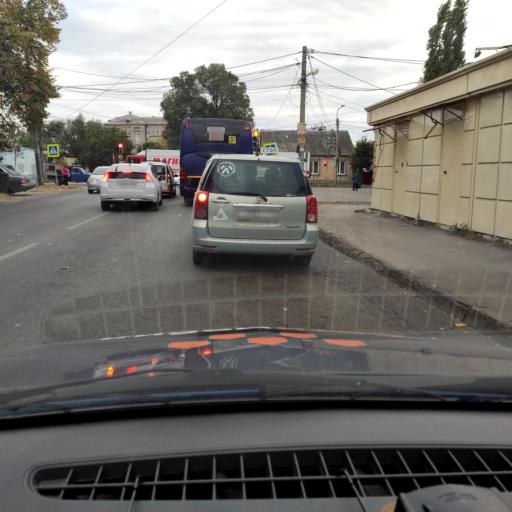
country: RU
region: Voronezj
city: Voronezh
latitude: 51.6345
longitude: 39.1891
